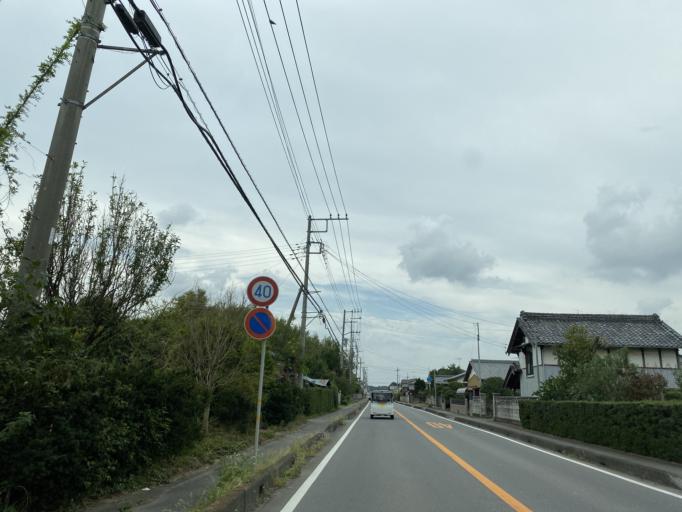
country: JP
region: Ibaraki
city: Moriya
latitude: 35.9648
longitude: 140.0211
